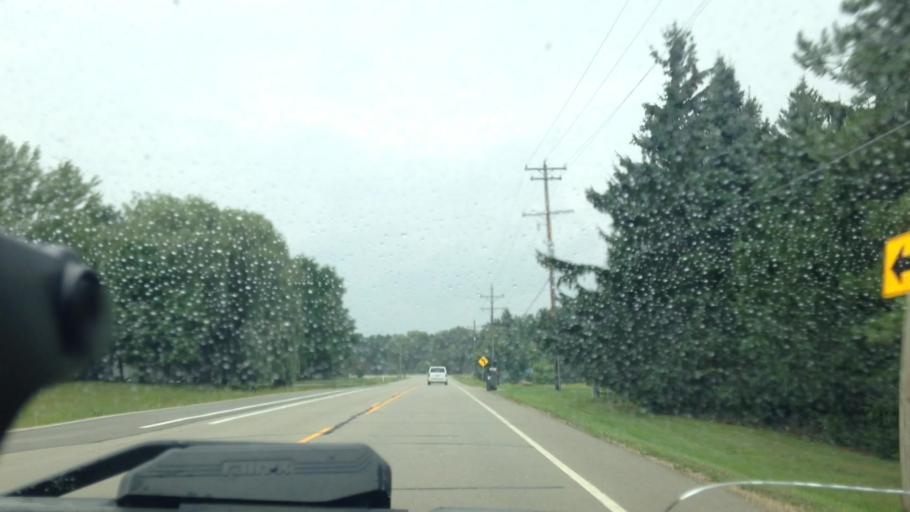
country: US
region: Wisconsin
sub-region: Washington County
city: Slinger
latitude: 43.3443
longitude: -88.3058
